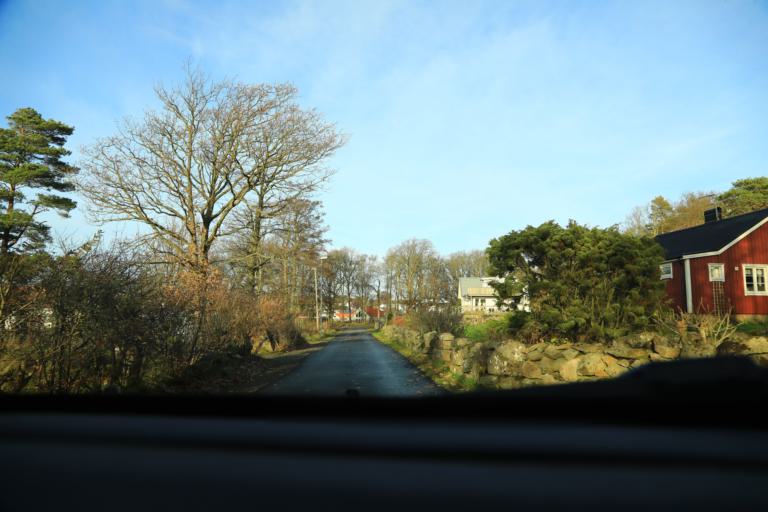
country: SE
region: Halland
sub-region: Varbergs Kommun
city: Varberg
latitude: 57.1884
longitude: 12.2124
